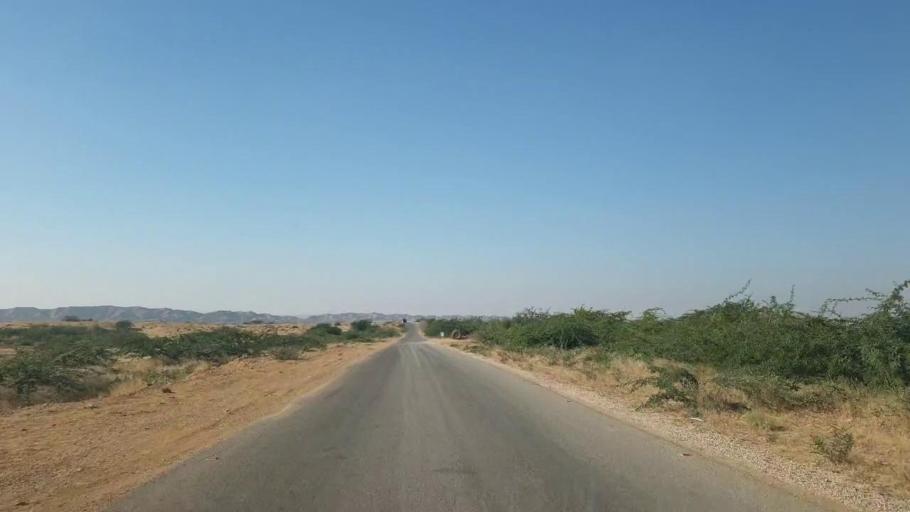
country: PK
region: Sindh
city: Malir Cantonment
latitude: 25.2801
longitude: 67.5846
